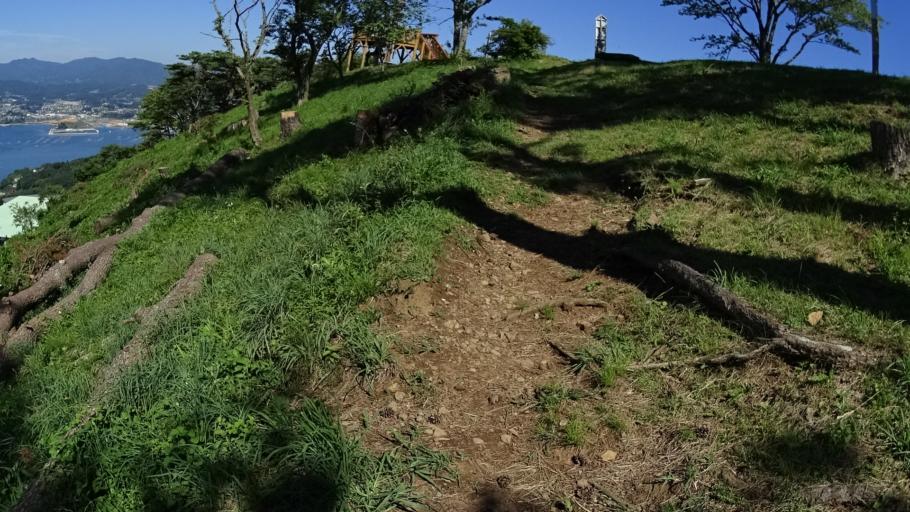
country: JP
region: Iwate
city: Ofunato
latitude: 38.8732
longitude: 141.6184
